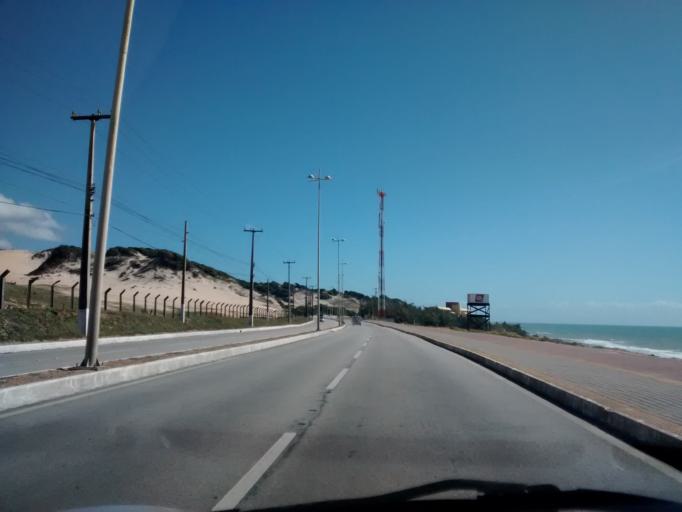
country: BR
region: Rio Grande do Norte
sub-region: Natal
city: Natal
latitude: -5.8476
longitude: -35.1822
